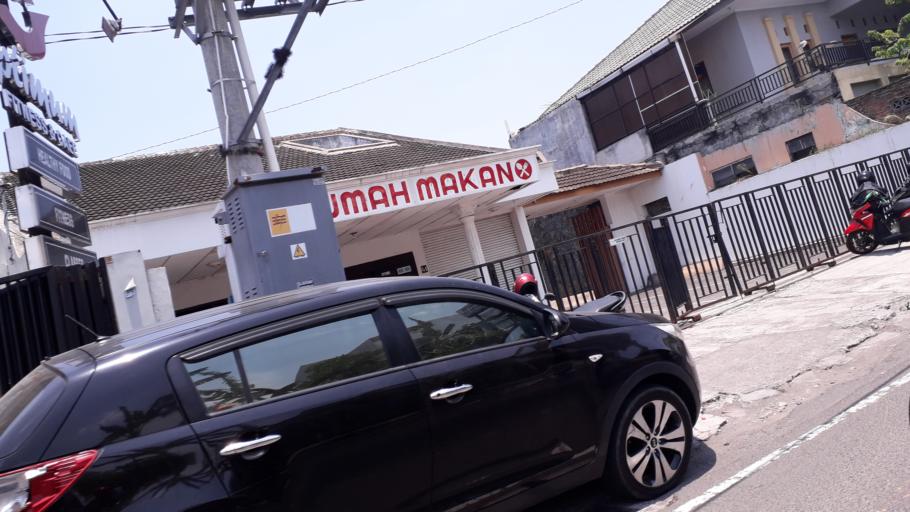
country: ID
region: Daerah Istimewa Yogyakarta
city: Yogyakarta
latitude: -7.7790
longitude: 110.3624
